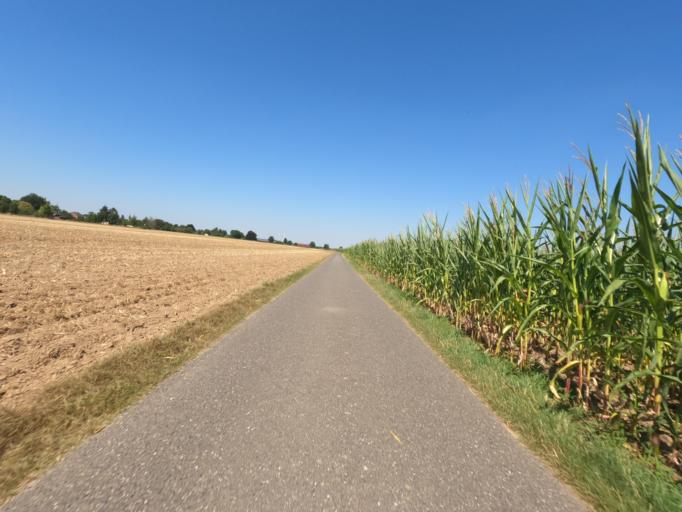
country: DE
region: North Rhine-Westphalia
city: Huckelhoven
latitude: 51.0969
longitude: 6.2447
